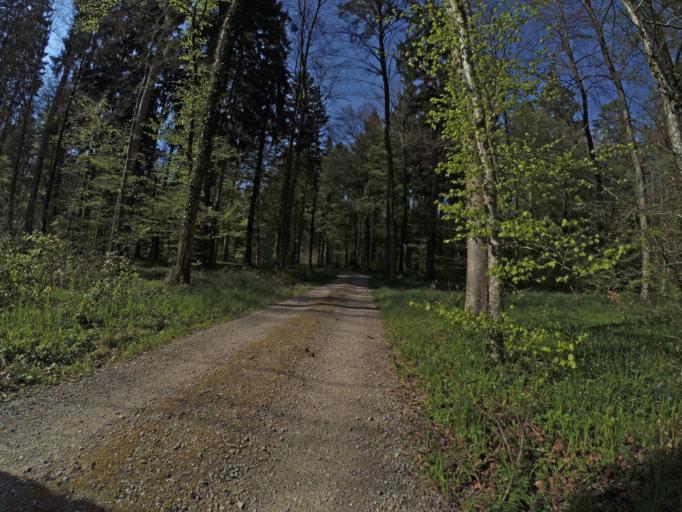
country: CH
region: Thurgau
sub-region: Frauenfeld District
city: Diessenhofen
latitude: 47.6528
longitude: 8.7590
